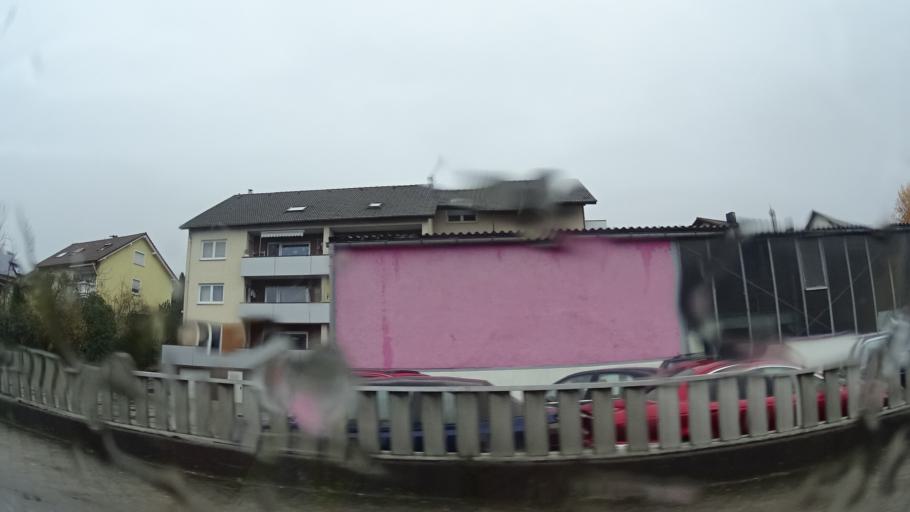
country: DE
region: Baden-Wuerttemberg
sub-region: Karlsruhe Region
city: Sinzheim
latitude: 48.7658
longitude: 8.1699
